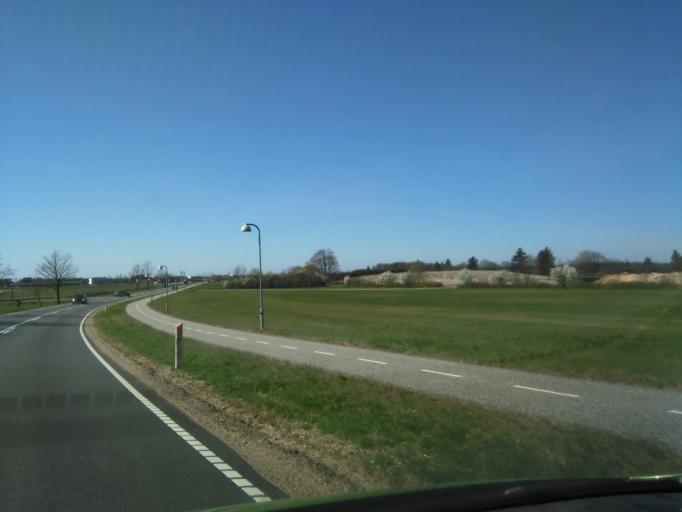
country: DK
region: South Denmark
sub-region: Billund Kommune
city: Billund
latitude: 55.7453
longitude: 9.1361
